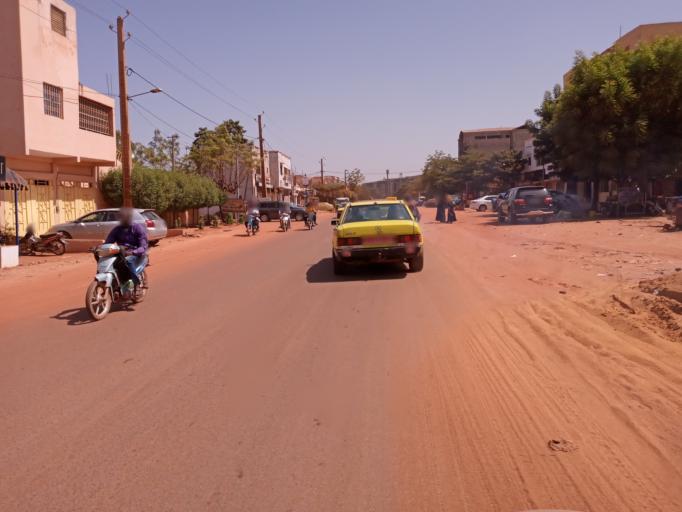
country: ML
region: Bamako
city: Bamako
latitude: 12.6140
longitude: -7.9967
